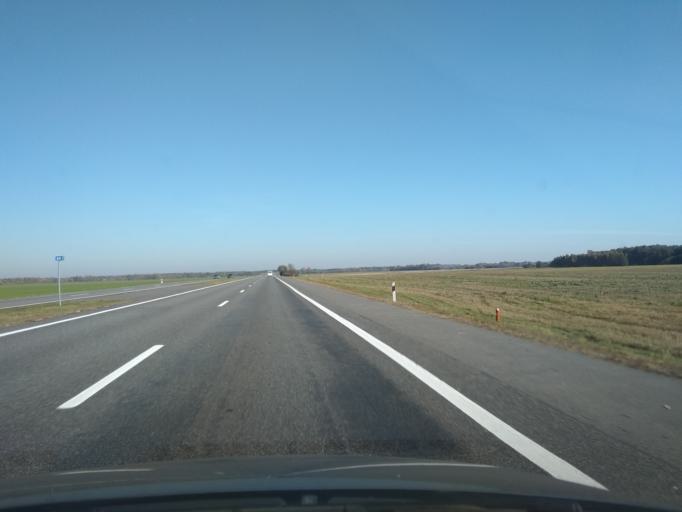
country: BY
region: Brest
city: Antopal'
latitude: 52.3180
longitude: 24.6133
